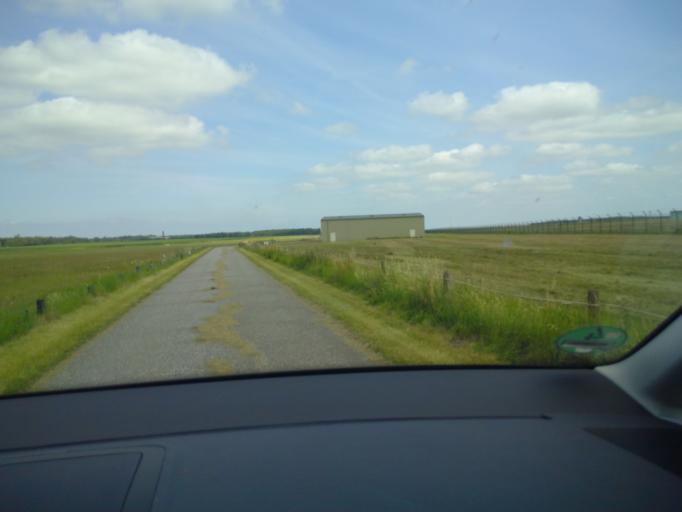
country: DE
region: Lower Saxony
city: Midlum
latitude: 53.7666
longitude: 8.6328
